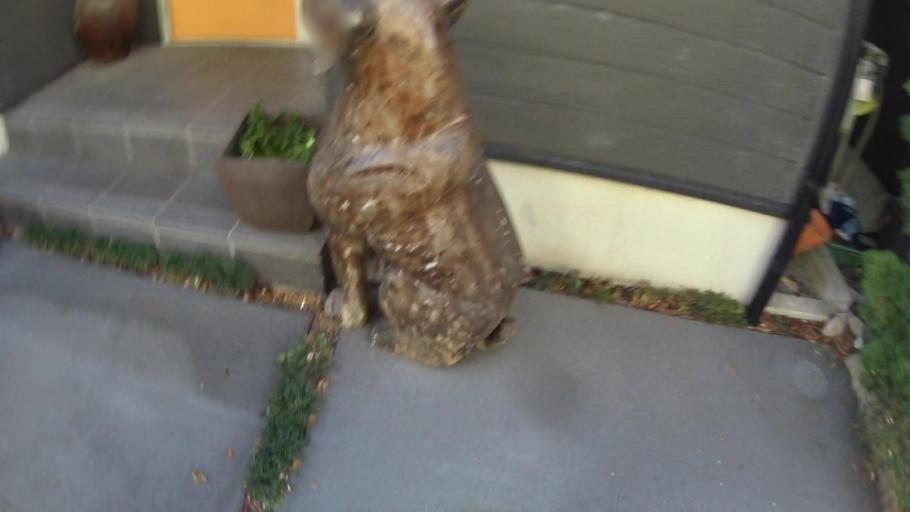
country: JP
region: Saitama
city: Yono
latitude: 35.8621
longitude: 139.6416
